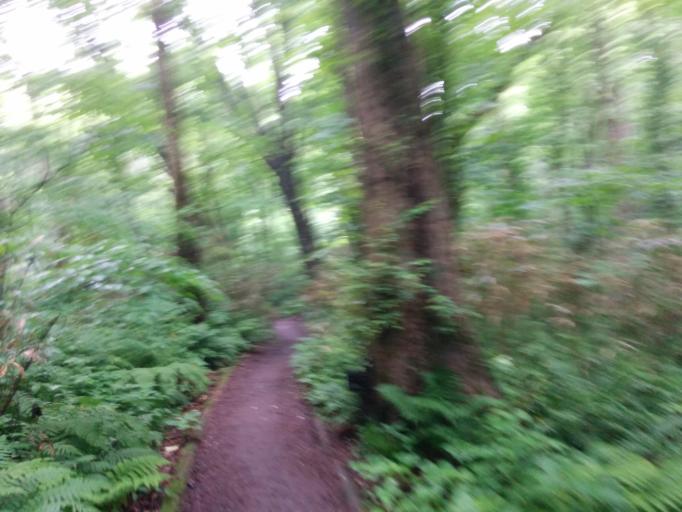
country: JP
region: Akita
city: Noshiromachi
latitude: 40.5621
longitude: 139.9811
